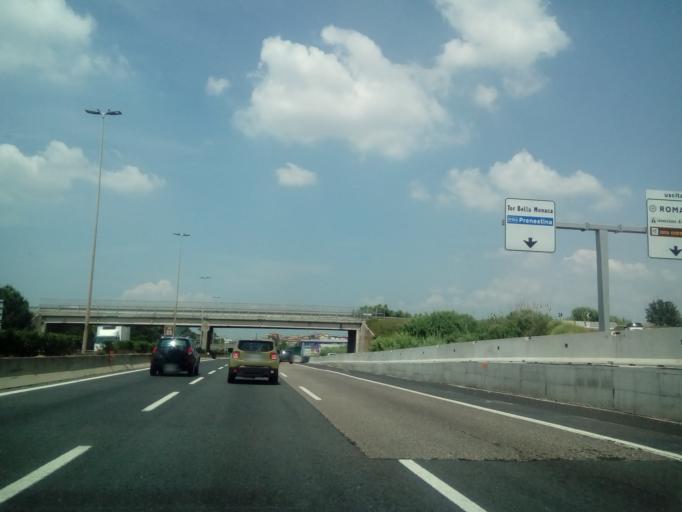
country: IT
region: Latium
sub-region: Citta metropolitana di Roma Capitale
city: Setteville
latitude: 41.8816
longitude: 12.6107
